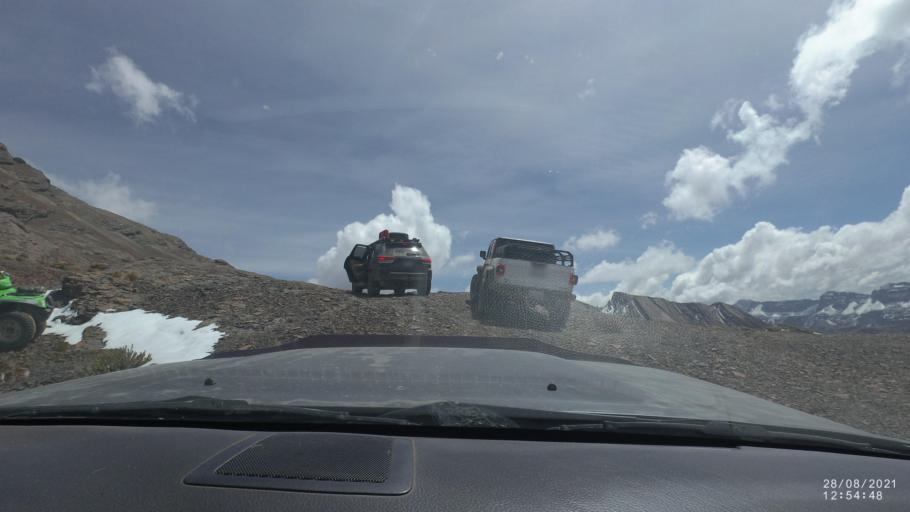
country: BO
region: Cochabamba
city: Sipe Sipe
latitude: -17.2836
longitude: -66.3856
